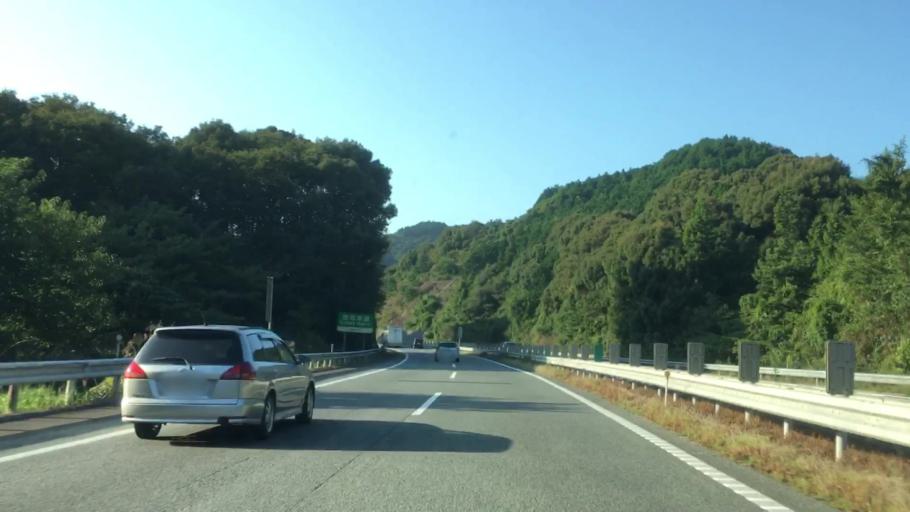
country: JP
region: Yamaguchi
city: Ogori-shimogo
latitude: 34.1339
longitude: 131.3757
